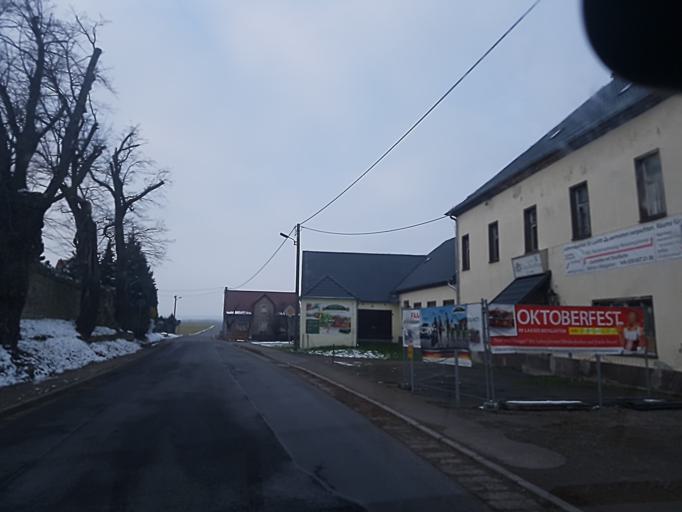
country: DE
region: Saxony
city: Cavertitz
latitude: 51.3668
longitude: 13.1462
